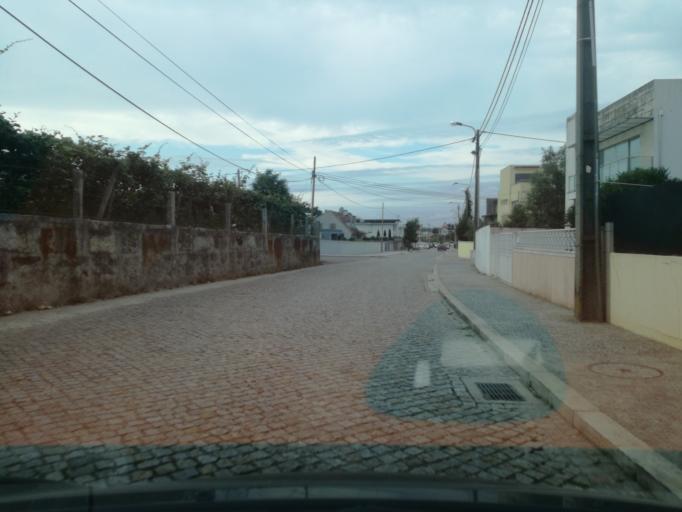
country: PT
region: Porto
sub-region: Maia
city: Maia
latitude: 41.2502
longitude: -8.6095
